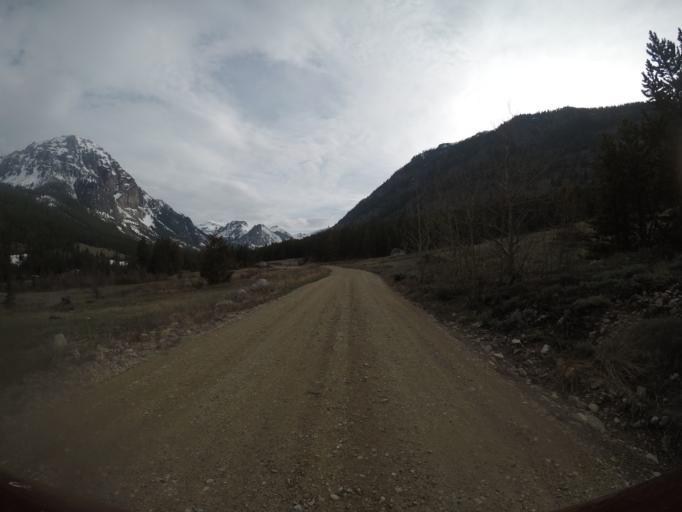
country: US
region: Montana
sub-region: Carbon County
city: Red Lodge
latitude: 45.0207
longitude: -109.4520
